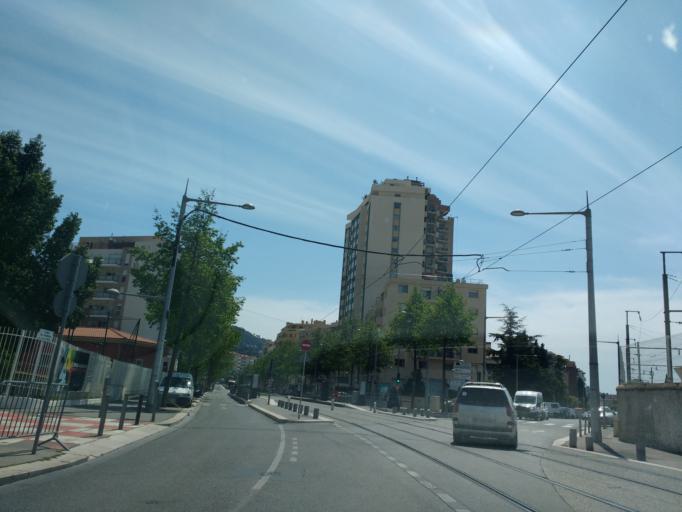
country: FR
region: Provence-Alpes-Cote d'Azur
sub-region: Departement des Alpes-Maritimes
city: Saint-Andre-de-la-Roche
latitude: 43.7191
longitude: 7.2916
